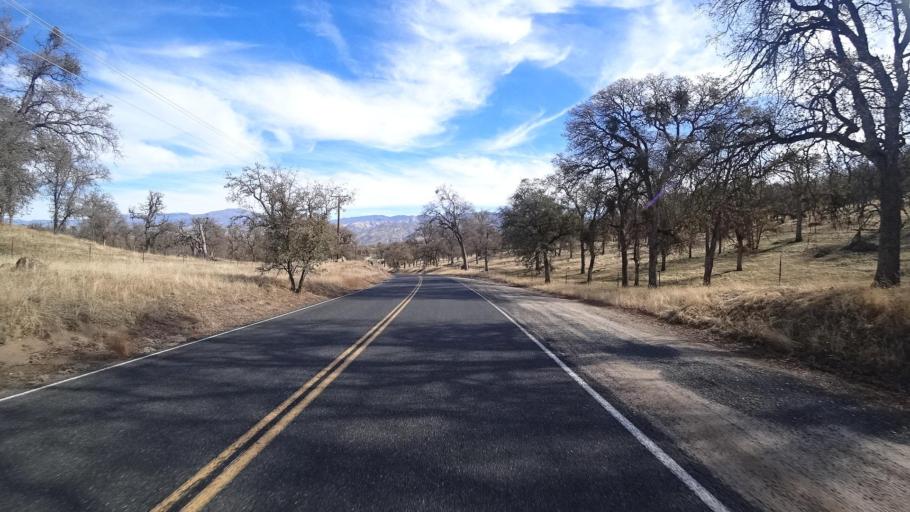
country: US
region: California
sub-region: Kern County
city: Alta Sierra
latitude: 35.6535
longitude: -118.7647
